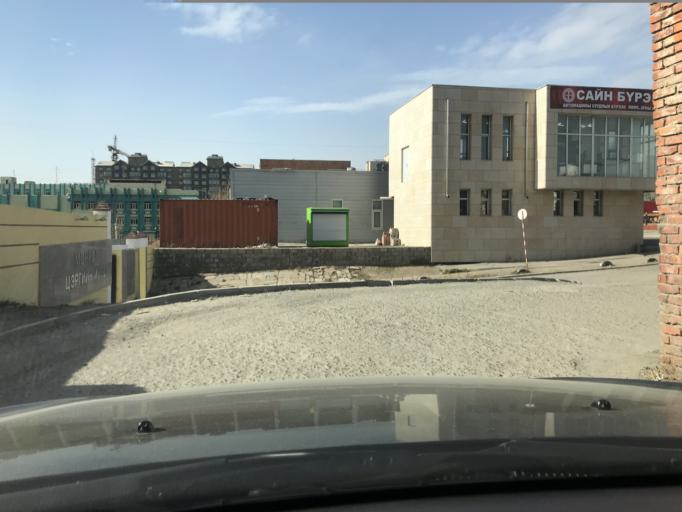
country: MN
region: Ulaanbaatar
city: Ulaanbaatar
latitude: 47.9232
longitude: 106.9537
